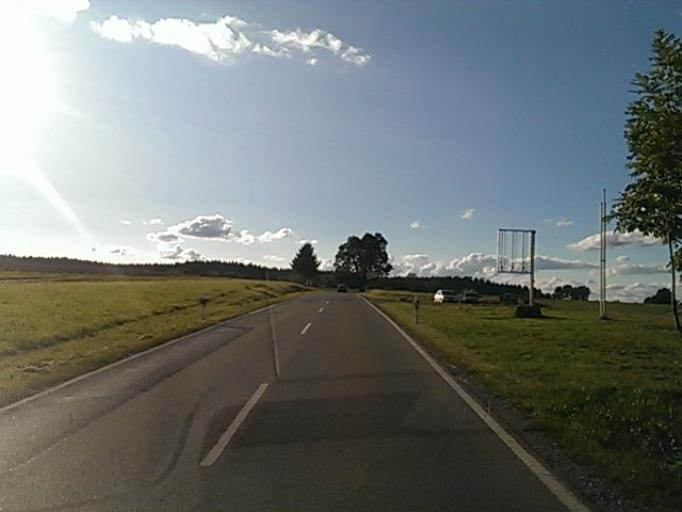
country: DE
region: Baden-Wuerttemberg
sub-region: Freiburg Region
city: Dornhan
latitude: 48.3067
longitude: 8.4796
